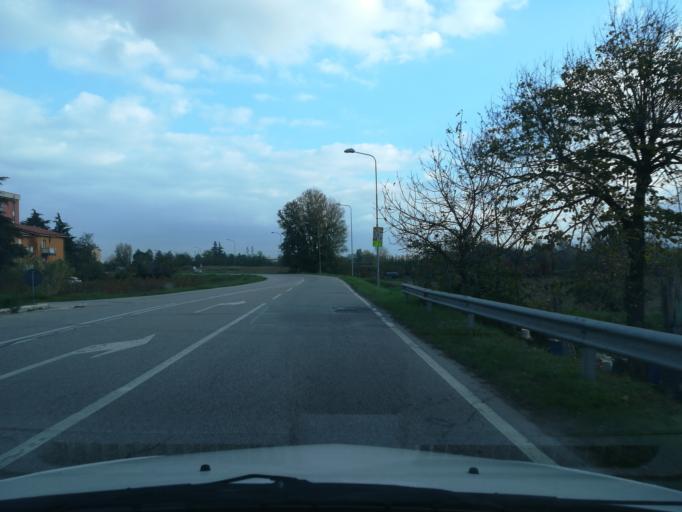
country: IT
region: Emilia-Romagna
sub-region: Provincia di Bologna
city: Imola
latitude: 44.3503
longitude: 11.7334
